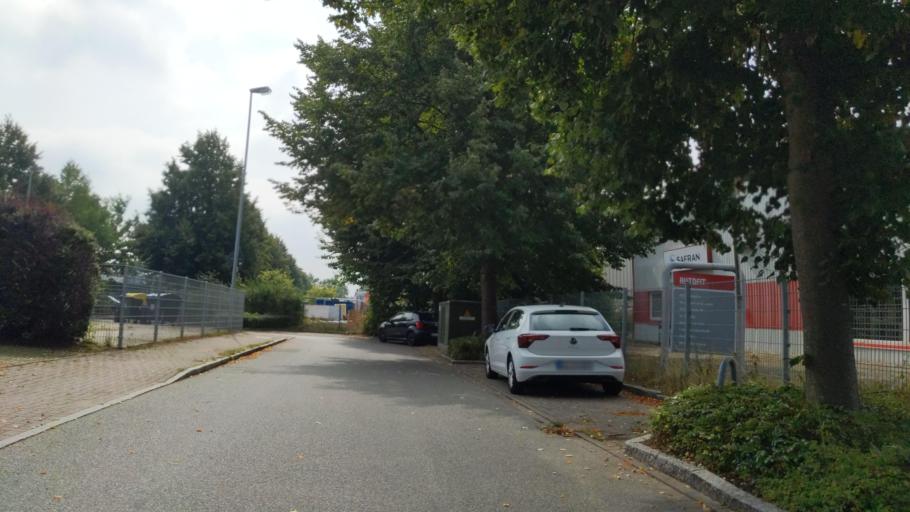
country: DE
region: Schleswig-Holstein
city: Stockelsdorf
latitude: 53.8943
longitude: 10.6232
